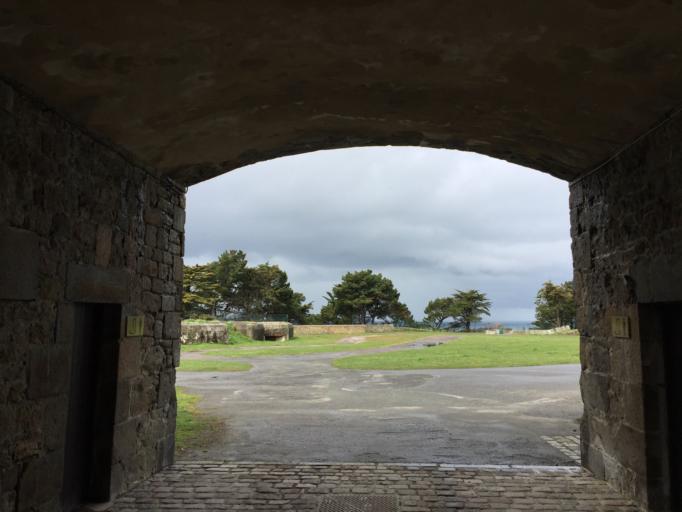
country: FR
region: Brittany
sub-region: Departement d'Ille-et-Vilaine
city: Saint-Malo
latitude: 48.6369
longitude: -2.0297
